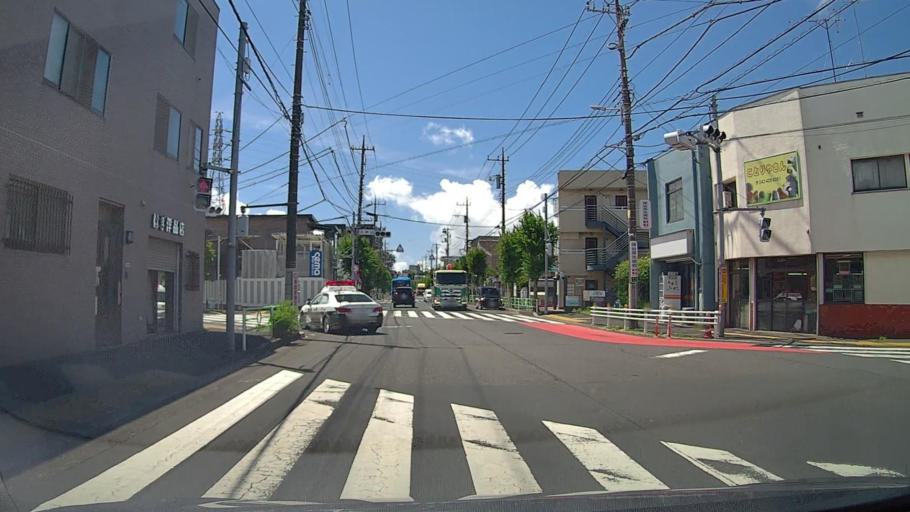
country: JP
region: Tokyo
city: Nishi-Tokyo-shi
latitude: 35.7383
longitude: 139.5659
